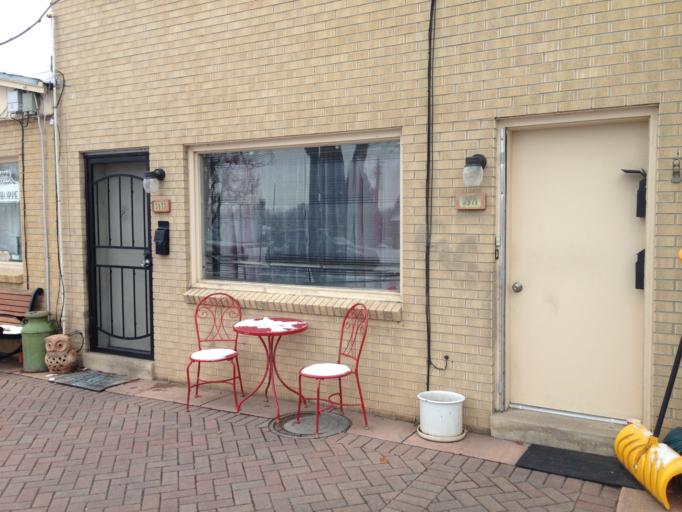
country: US
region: Colorado
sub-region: Adams County
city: Westminster
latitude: 39.8292
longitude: -105.0400
